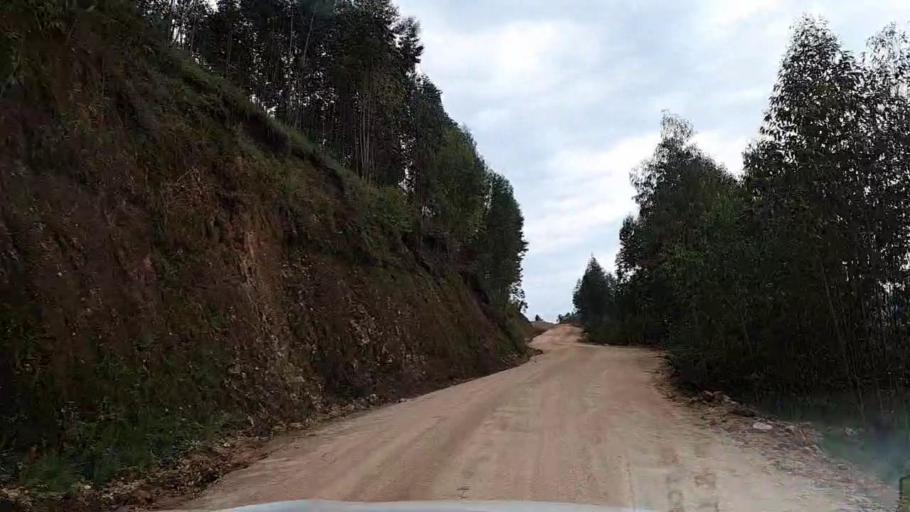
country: RW
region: Southern Province
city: Nzega
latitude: -2.3693
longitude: 29.4505
